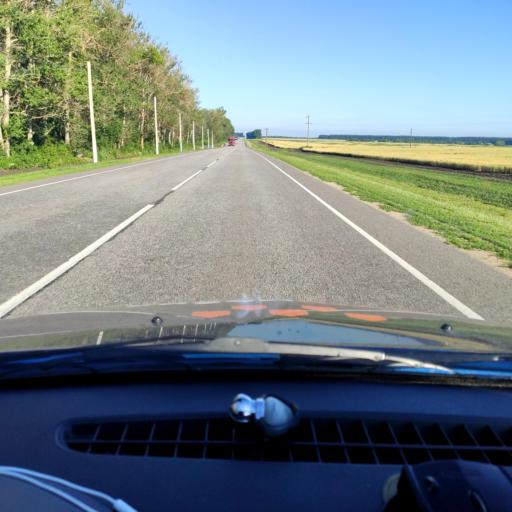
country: RU
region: Orjol
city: Pokrovskoye
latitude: 52.6296
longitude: 36.7053
